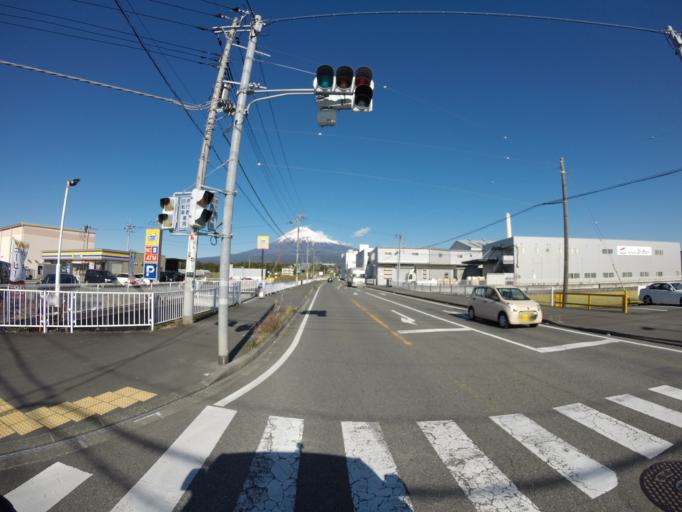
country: JP
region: Shizuoka
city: Fuji
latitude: 35.1731
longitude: 138.6560
